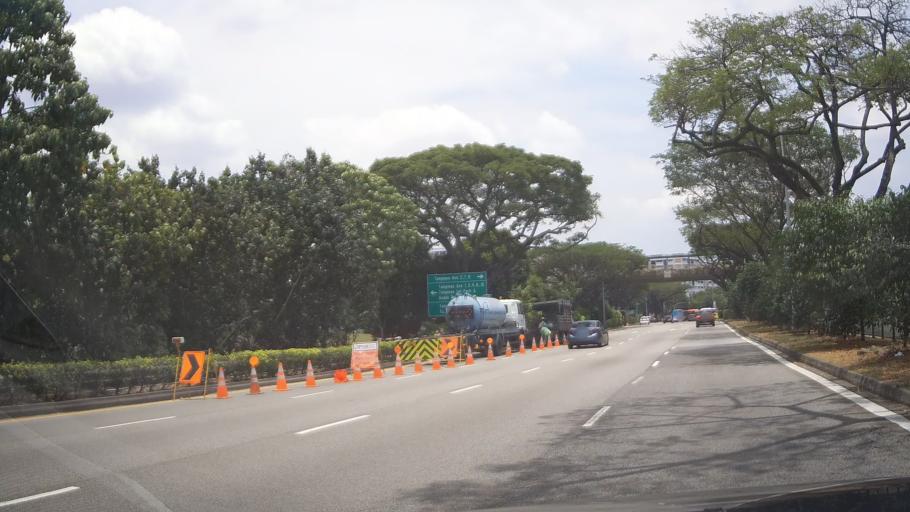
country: SG
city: Singapore
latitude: 1.3445
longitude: 103.9445
